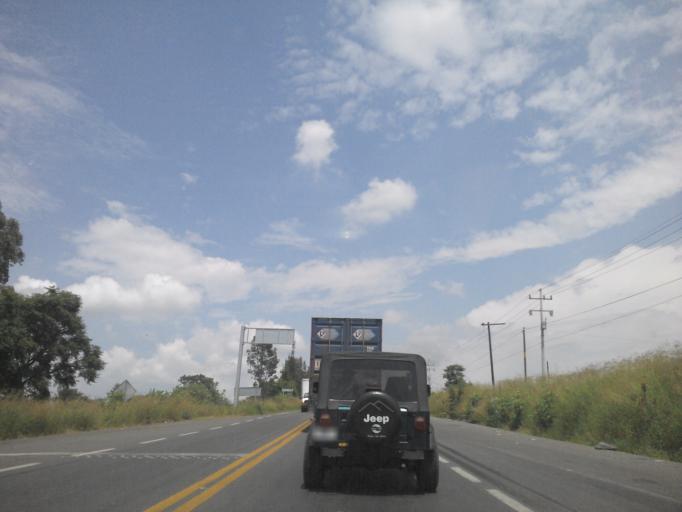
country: MX
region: Jalisco
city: Zapotlanejo
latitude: 20.6822
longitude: -103.0004
